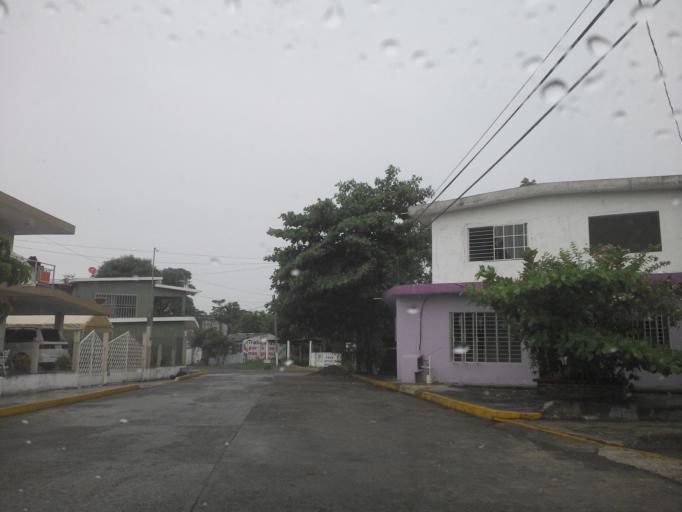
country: MX
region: Veracruz
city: Nautla
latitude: 20.2103
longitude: -96.7755
